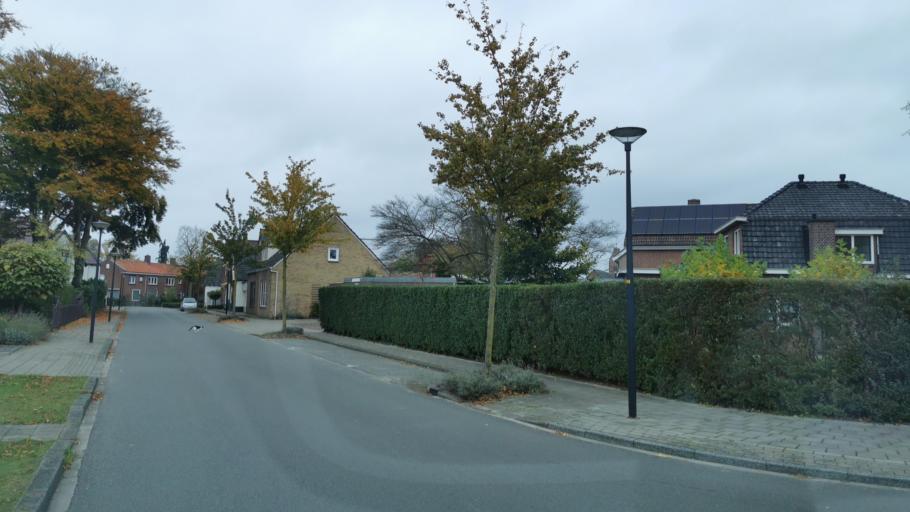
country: DE
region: North Rhine-Westphalia
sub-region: Regierungsbezirk Munster
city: Gronau
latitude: 52.2126
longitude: 6.9755
